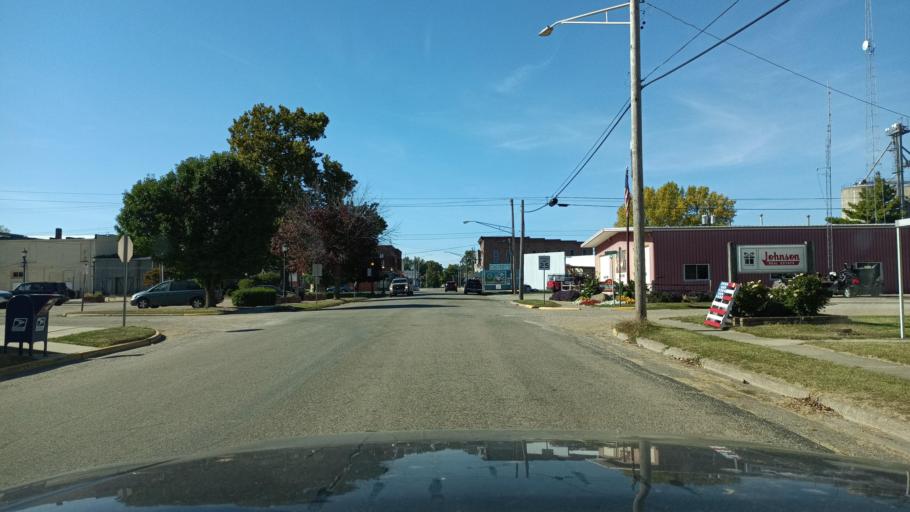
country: US
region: Illinois
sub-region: Logan County
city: Atlanta
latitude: 40.2603
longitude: -89.2300
